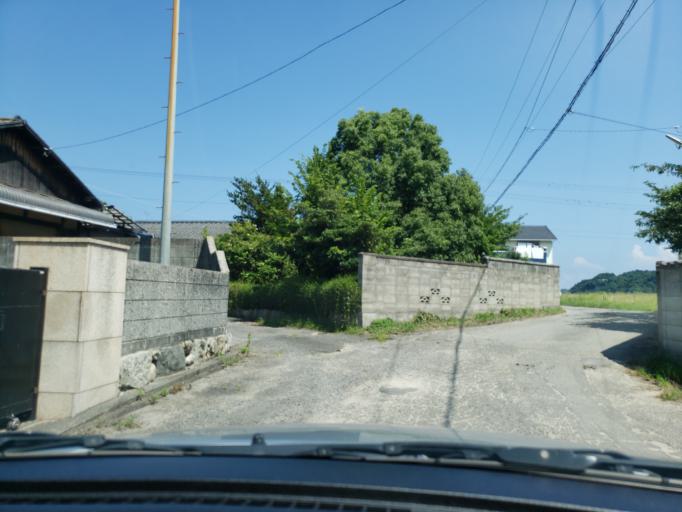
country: JP
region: Ehime
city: Hojo
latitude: 34.0865
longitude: 132.9291
